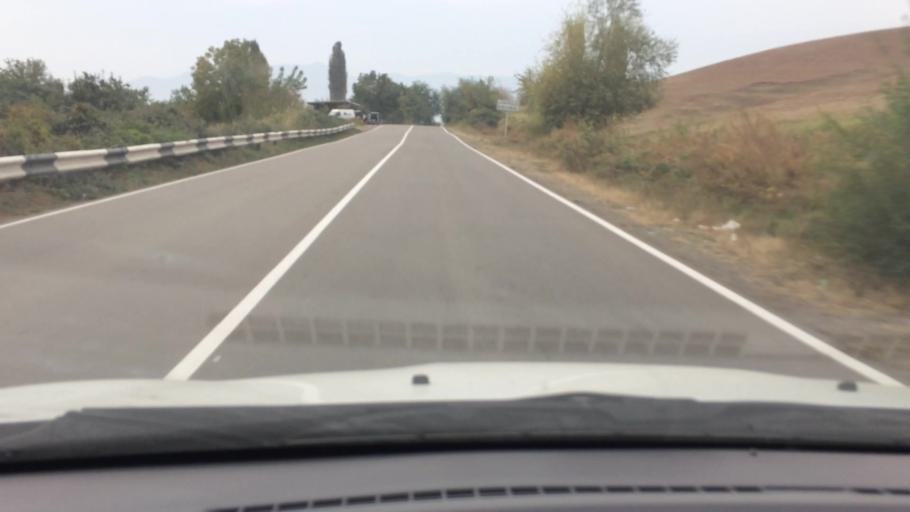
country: AM
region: Tavush
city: Bagratashen
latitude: 41.2831
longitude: 44.7907
